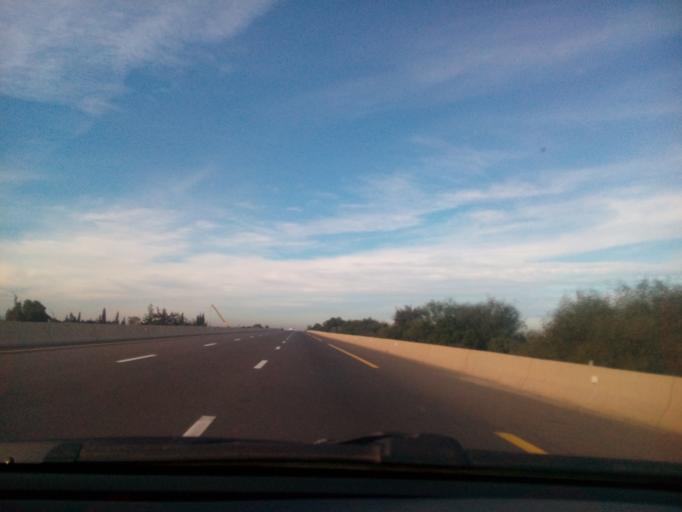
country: DZ
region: Mascara
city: Mascara
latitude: 35.6225
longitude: 0.0657
